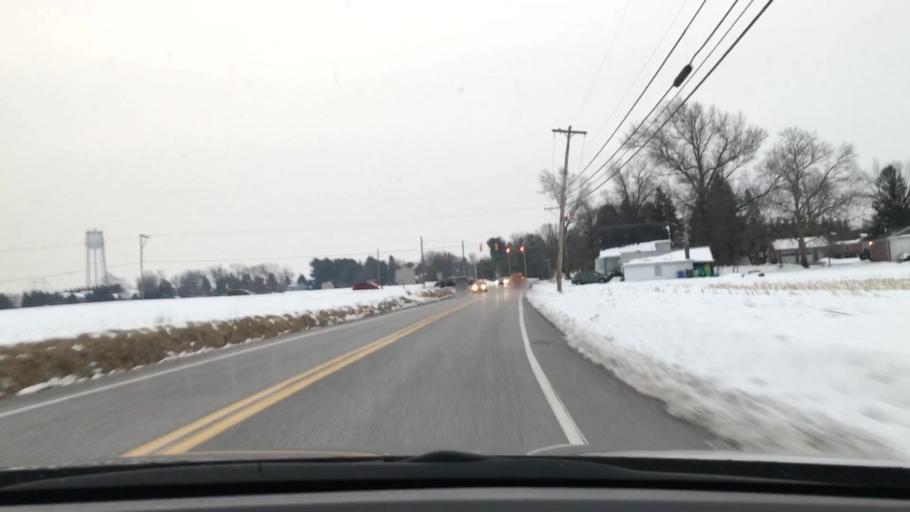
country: US
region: Pennsylvania
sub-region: York County
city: Dover
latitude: 39.9802
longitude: -76.8502
